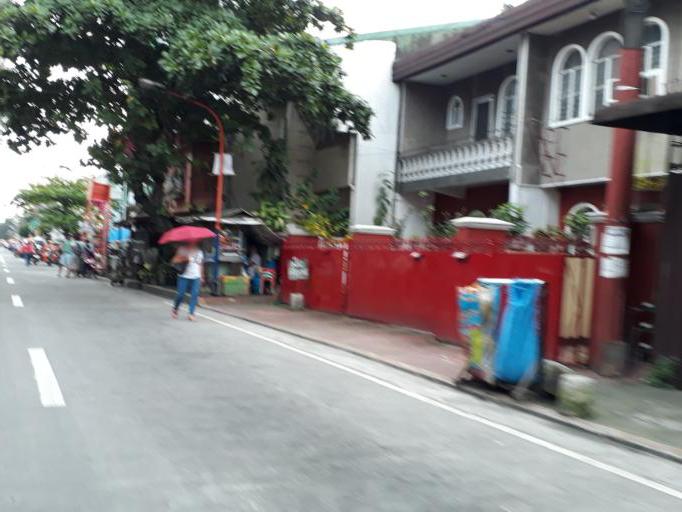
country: PH
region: Metro Manila
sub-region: City of Manila
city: Manila
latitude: 14.6113
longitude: 120.9955
